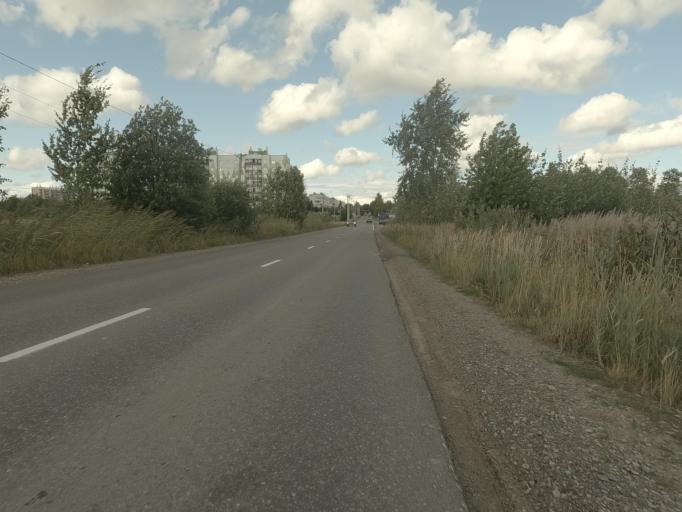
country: RU
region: Leningrad
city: Shcheglovo
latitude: 60.0229
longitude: 30.7488
